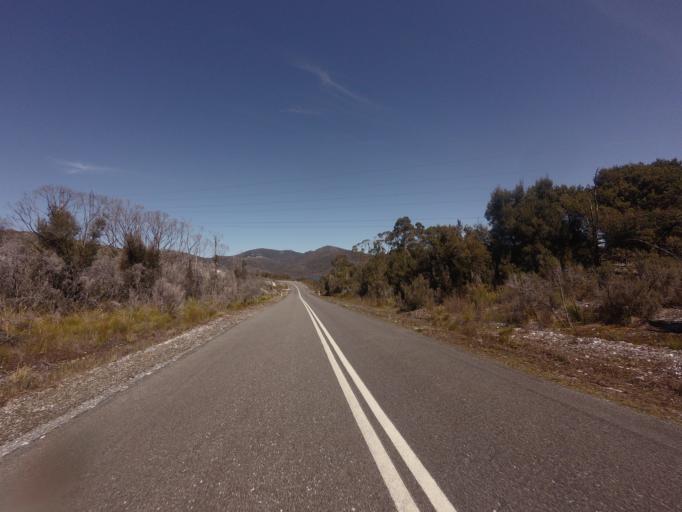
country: AU
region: Tasmania
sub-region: Huon Valley
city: Geeveston
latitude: -42.8373
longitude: 146.1575
